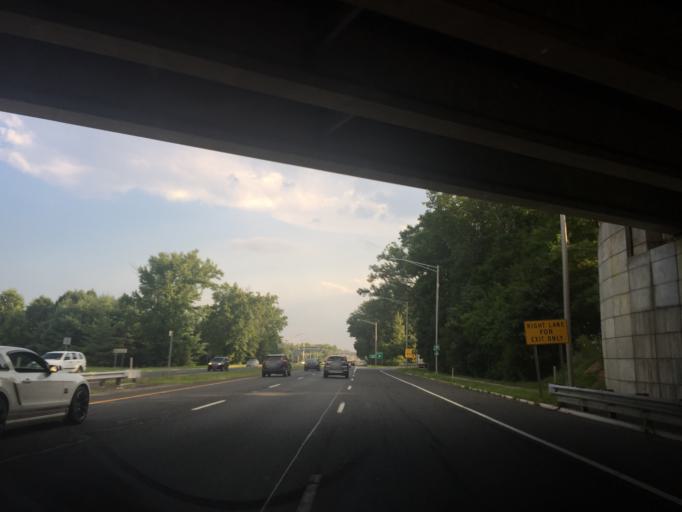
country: US
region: New Jersey
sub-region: Mercer County
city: Hightstown
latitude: 40.2827
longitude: -74.5292
